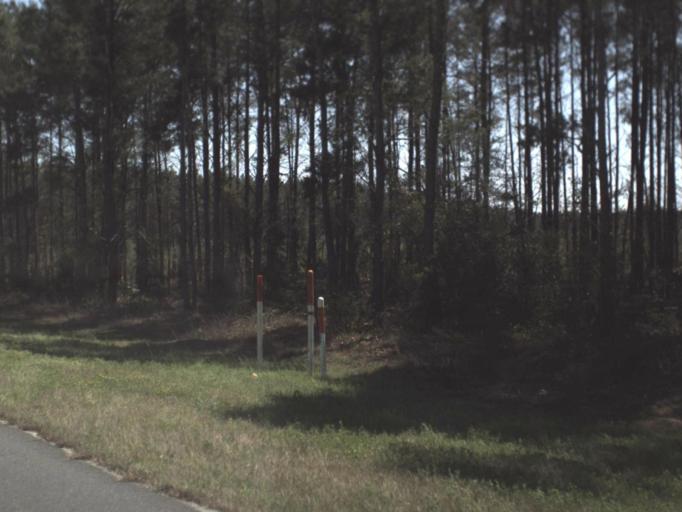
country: US
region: Florida
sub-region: Bay County
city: Youngstown
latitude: 30.4316
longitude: -85.3288
